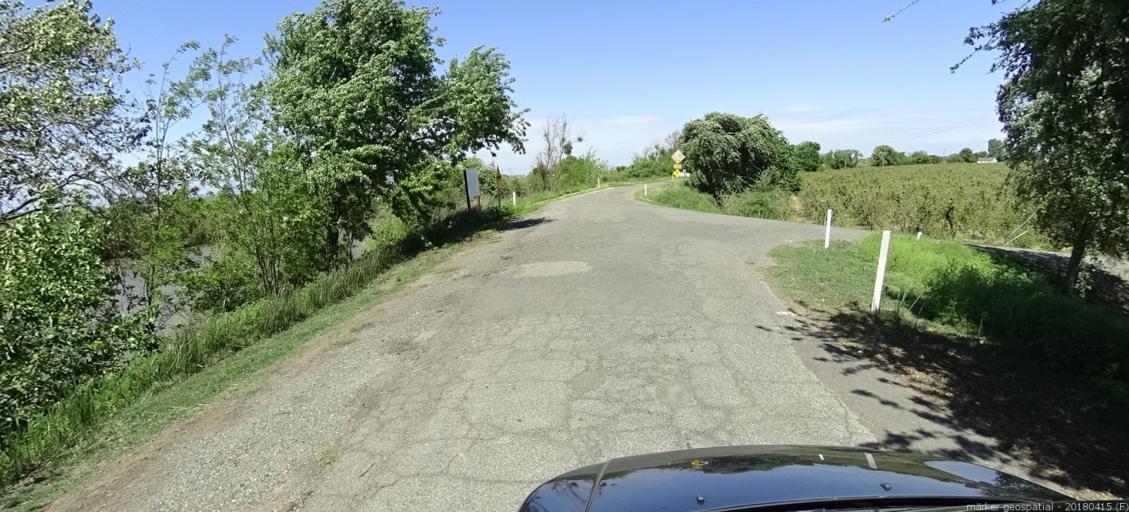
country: US
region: California
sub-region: Sacramento County
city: Walnut Grove
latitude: 38.2955
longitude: -121.6048
